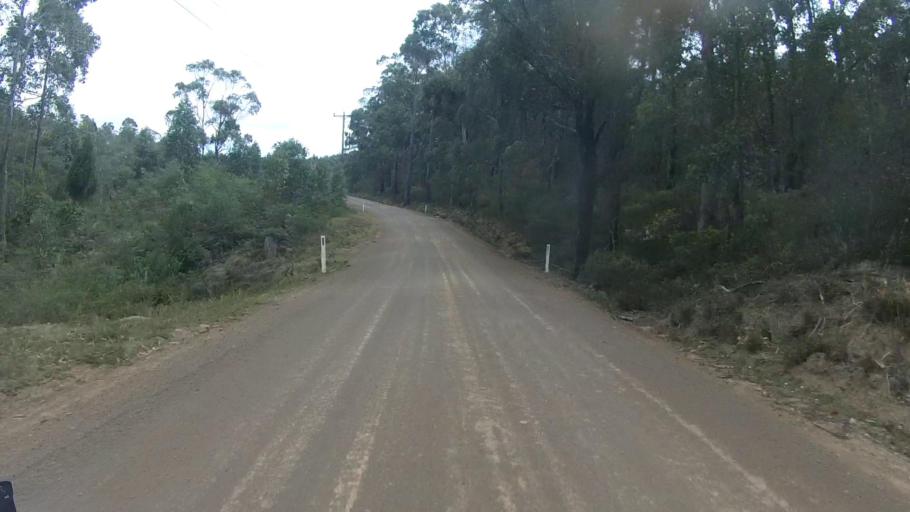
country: AU
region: Tasmania
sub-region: Sorell
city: Sorell
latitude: -42.7616
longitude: 147.8025
